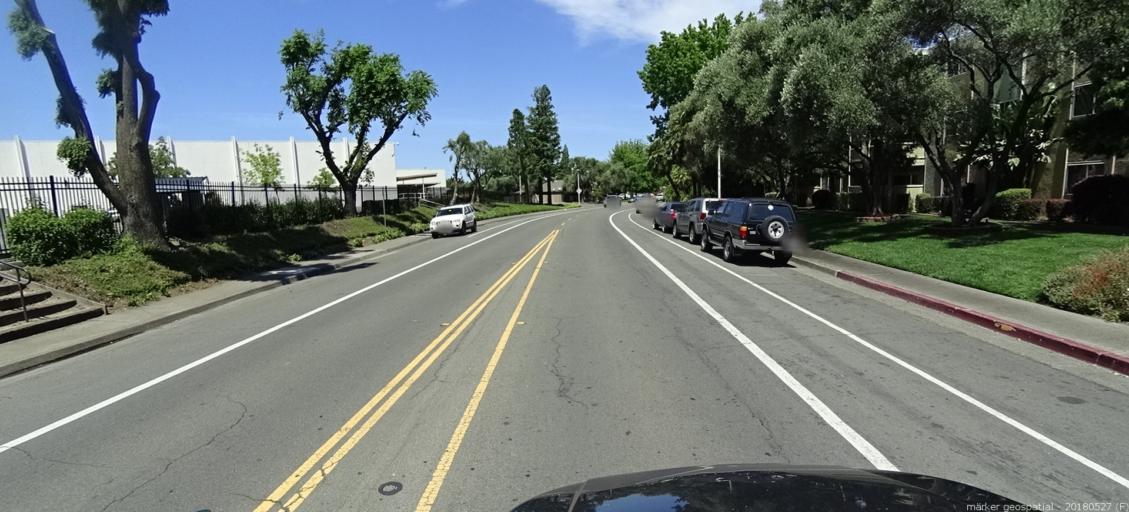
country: US
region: California
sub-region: Sacramento County
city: Rosemont
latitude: 38.5488
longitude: -121.3935
